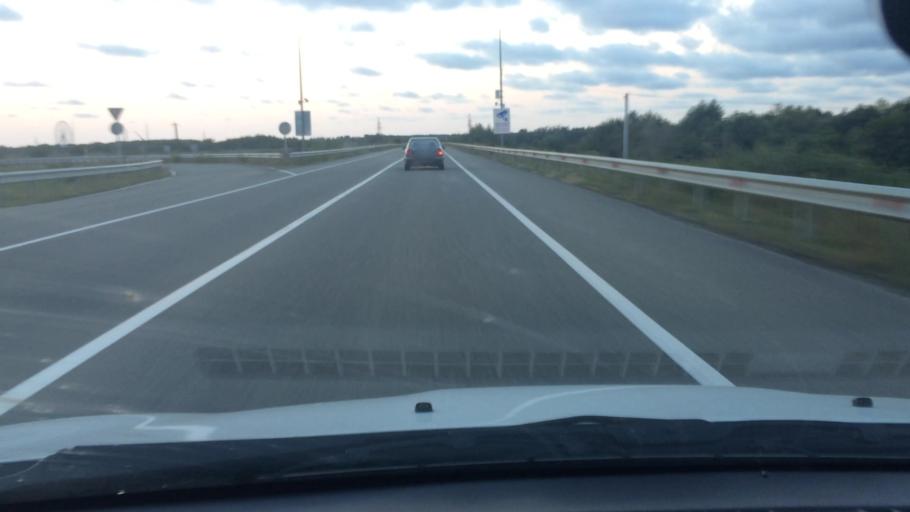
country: GE
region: Ajaria
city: Ochkhamuri
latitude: 41.9004
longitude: 41.7950
